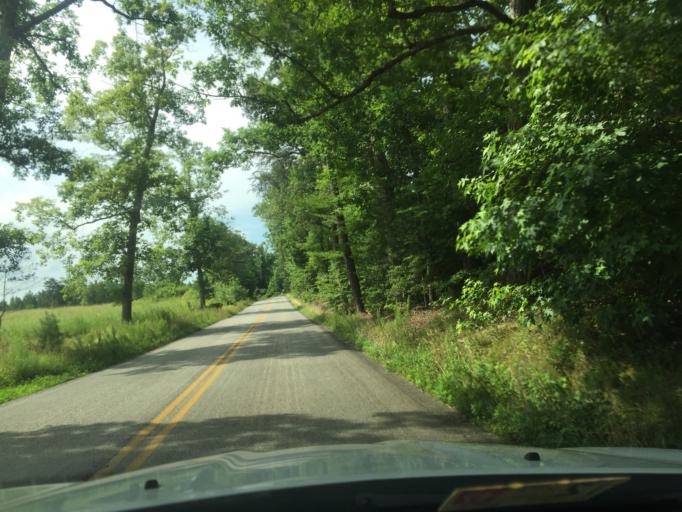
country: US
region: Virginia
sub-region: Charles City County
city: Charles City
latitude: 37.3920
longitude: -77.0154
